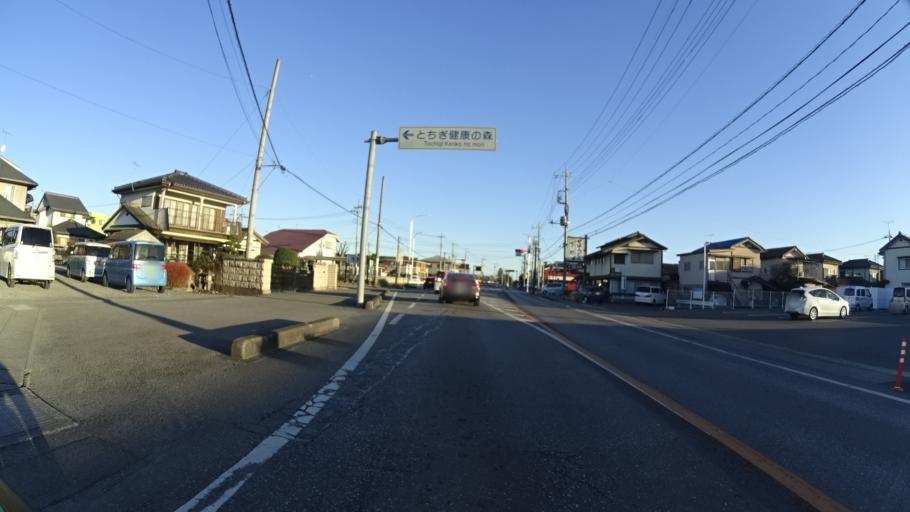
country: JP
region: Tochigi
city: Utsunomiya-shi
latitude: 36.5816
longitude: 139.8391
